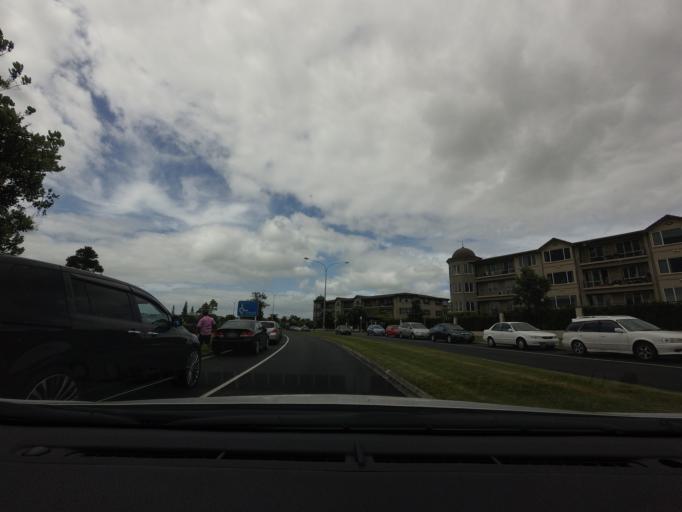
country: NZ
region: Auckland
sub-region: Auckland
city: Rothesay Bay
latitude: -36.5837
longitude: 174.6858
